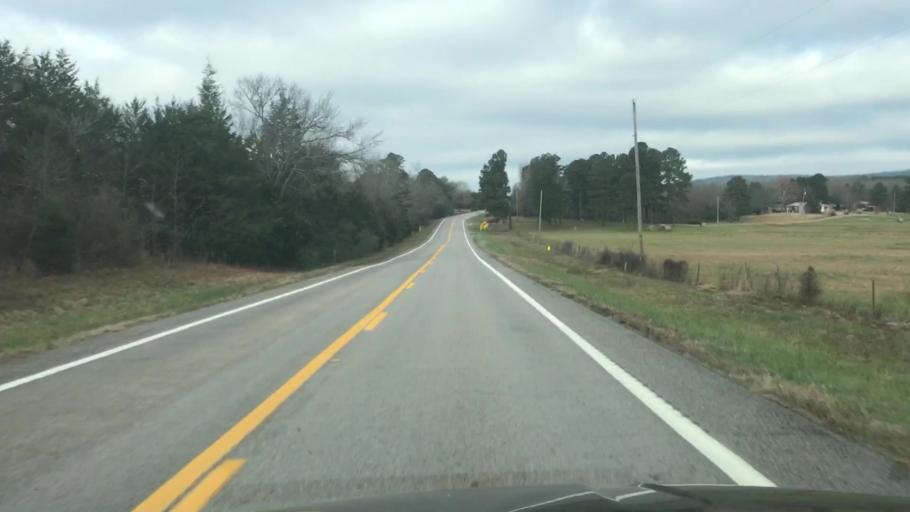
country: US
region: Arkansas
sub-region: Montgomery County
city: Mount Ida
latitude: 34.6499
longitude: -93.7523
